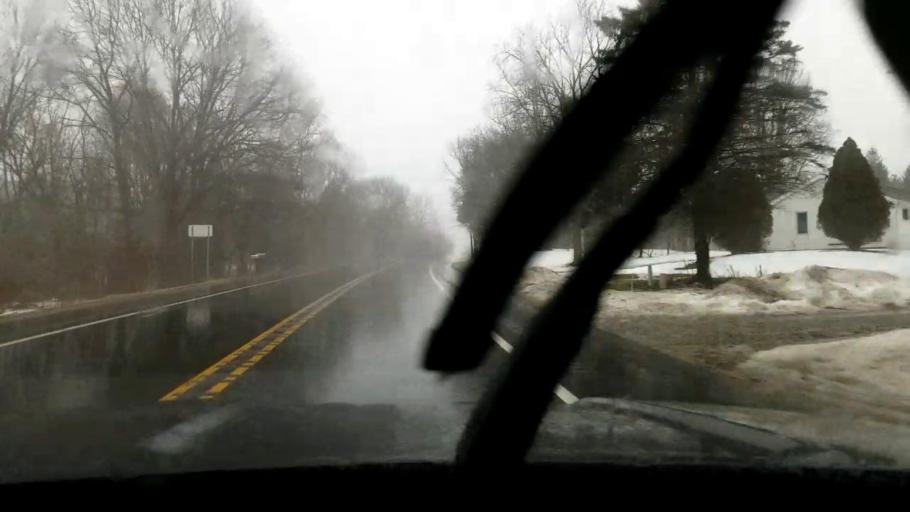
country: US
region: Michigan
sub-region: Jackson County
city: Michigan Center
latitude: 42.1851
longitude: -84.2989
